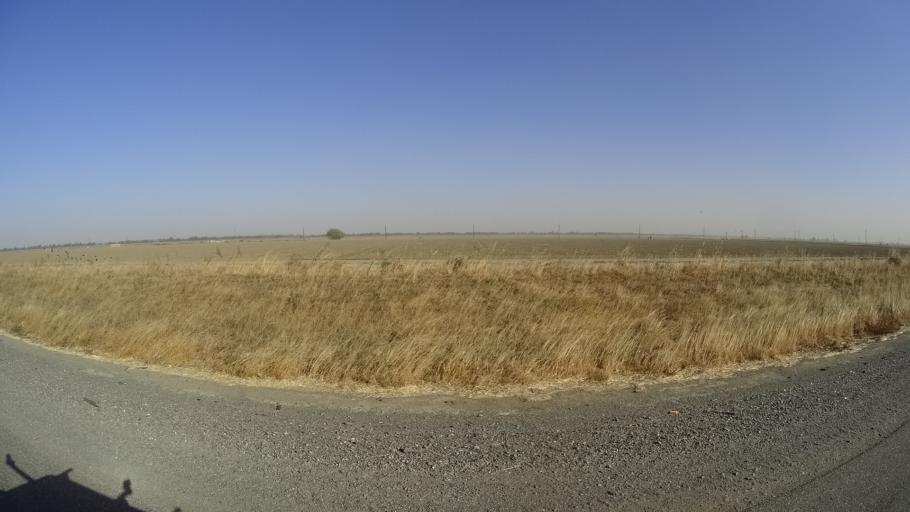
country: US
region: California
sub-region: Yolo County
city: Woodland
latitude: 38.7720
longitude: -121.7287
